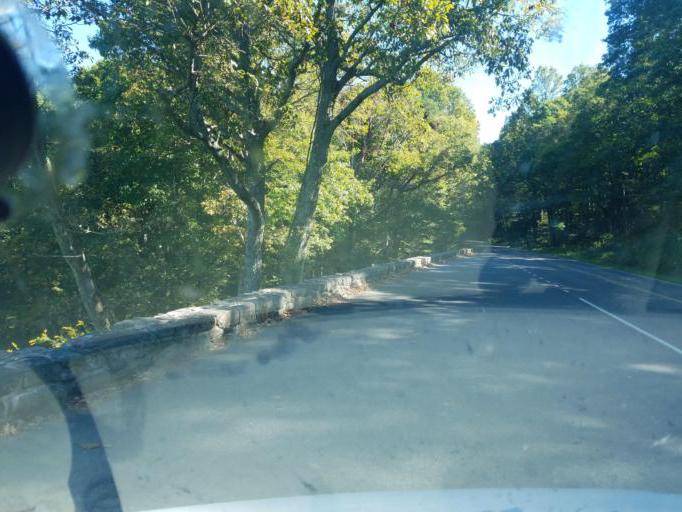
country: US
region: Virginia
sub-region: Rockingham County
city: Elkton
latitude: 38.3678
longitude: -78.5365
